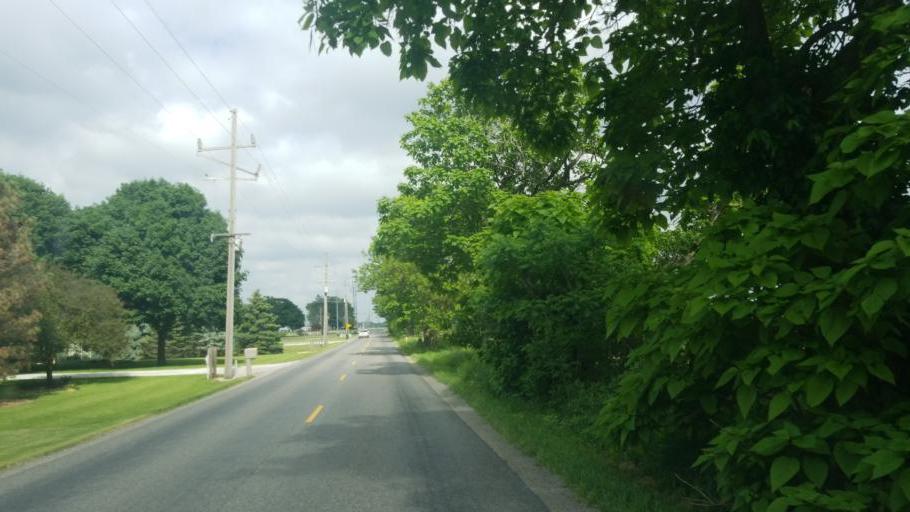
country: US
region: Indiana
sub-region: Elkhart County
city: Wakarusa
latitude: 41.4933
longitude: -86.0057
